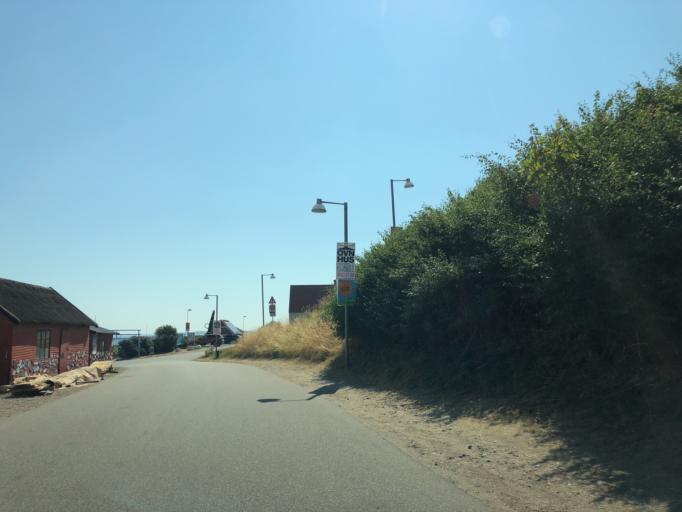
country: DK
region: Zealand
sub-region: Odsherred Kommune
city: Asnaes
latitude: 55.9719
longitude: 11.3674
